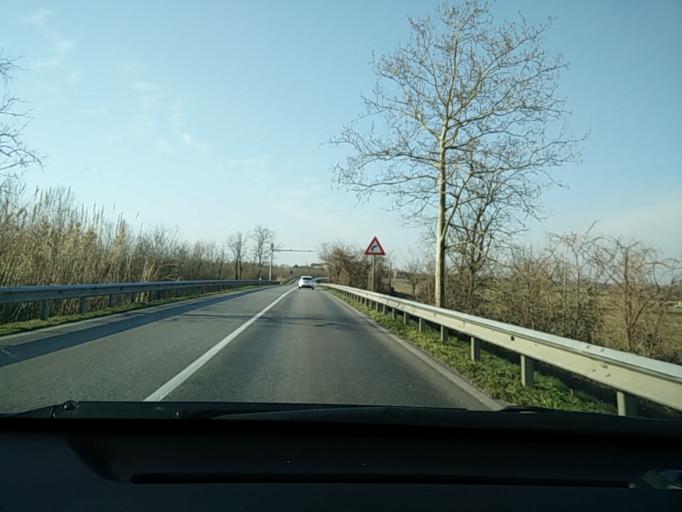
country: IT
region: Veneto
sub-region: Provincia di Venezia
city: Quarto d'Altino
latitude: 45.5377
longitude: 12.3993
